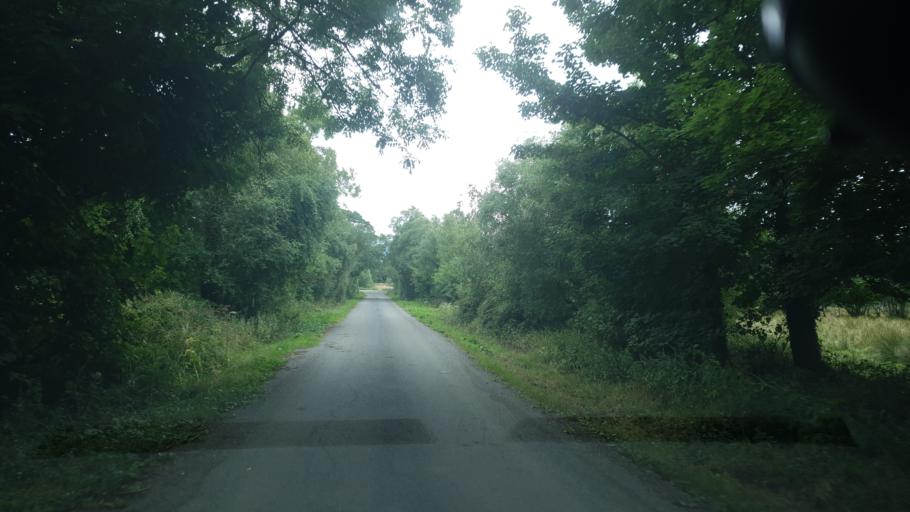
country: IE
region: Munster
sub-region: Ciarrai
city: Cill Airne
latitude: 52.1102
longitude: -9.4710
